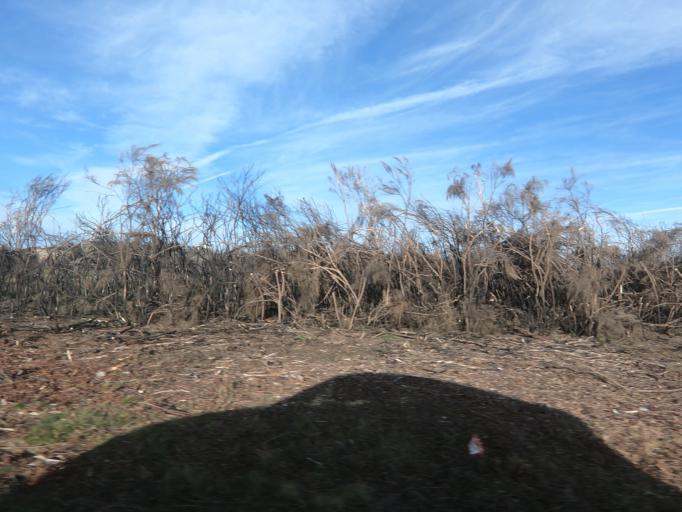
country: PT
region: Vila Real
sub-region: Sabrosa
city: Sabrosa
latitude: 41.2962
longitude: -7.6090
